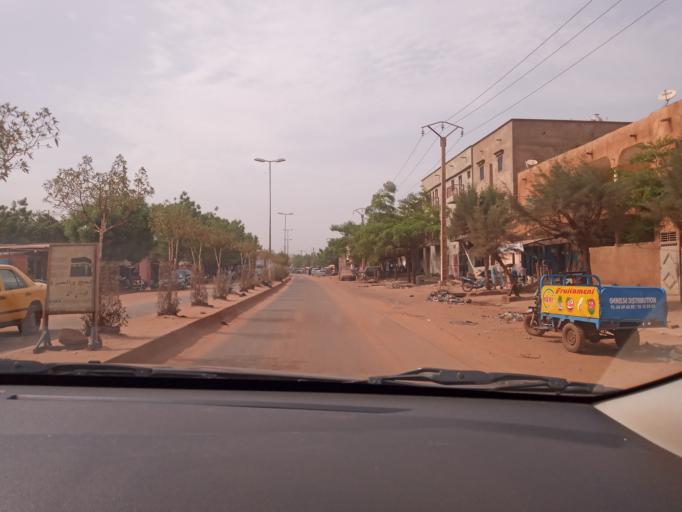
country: ML
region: Bamako
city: Bamako
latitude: 12.6722
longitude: -7.9241
